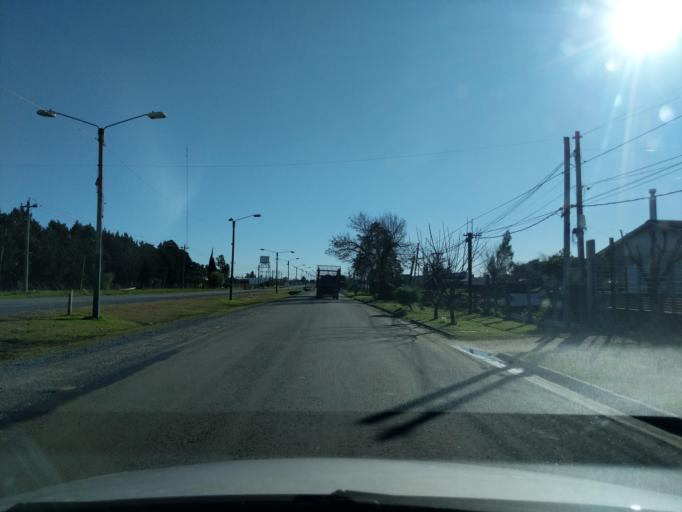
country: UY
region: Florida
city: Florida
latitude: -34.0902
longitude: -56.2383
